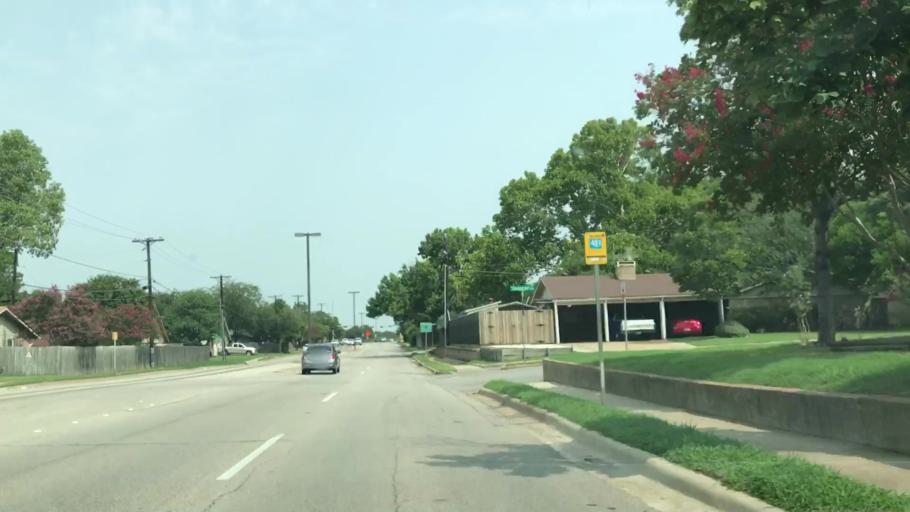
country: US
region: Texas
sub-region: Dallas County
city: Irving
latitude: 32.8564
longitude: -96.9590
